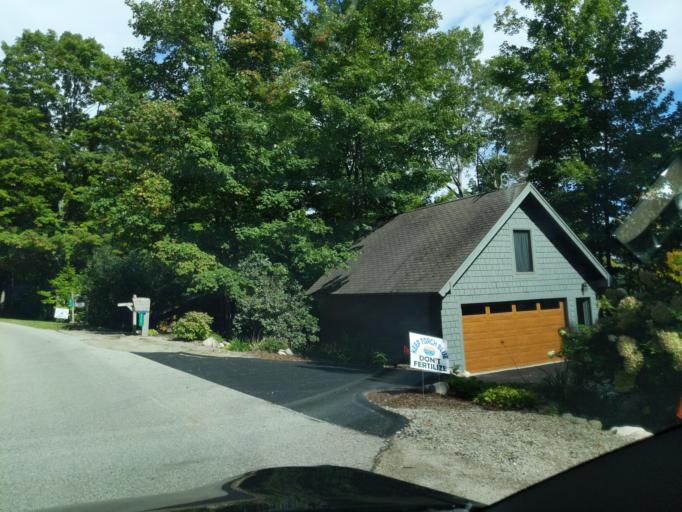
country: US
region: Michigan
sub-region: Antrim County
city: Bellaire
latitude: 44.9718
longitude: -85.3234
